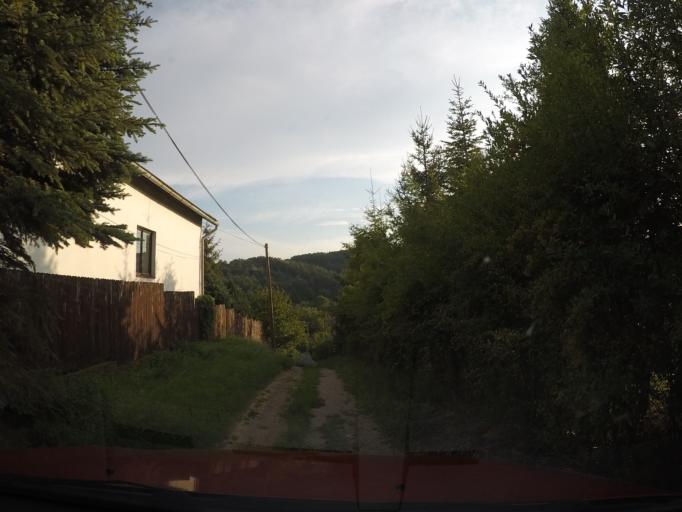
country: SK
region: Kosicky
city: Kosice
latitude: 48.7057
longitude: 21.2148
